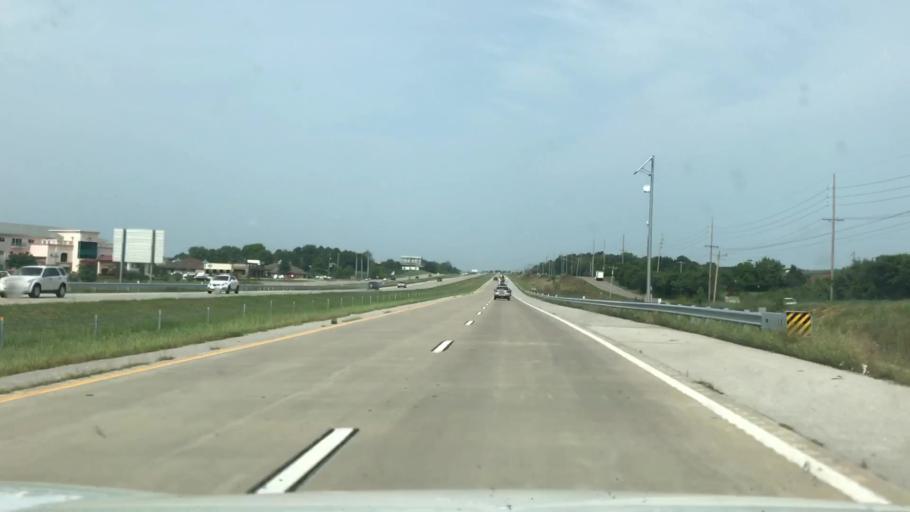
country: US
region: Missouri
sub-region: Saint Charles County
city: Dardenne Prairie
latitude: 38.7601
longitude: -90.7158
